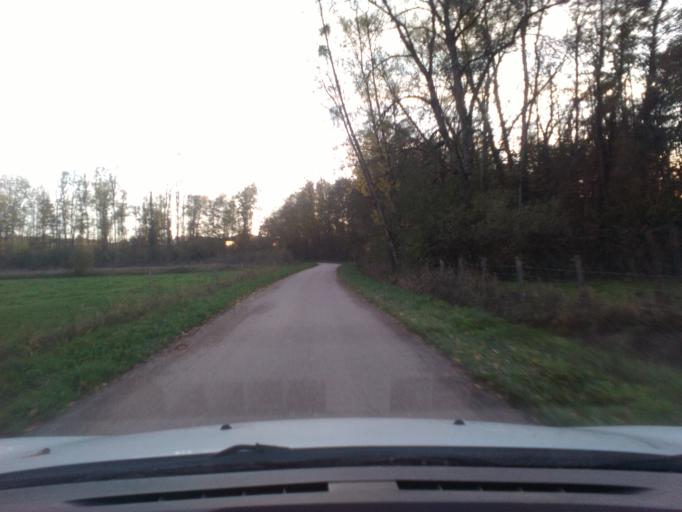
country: FR
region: Lorraine
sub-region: Departement des Vosges
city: Mirecourt
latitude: 48.2593
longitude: 6.1742
